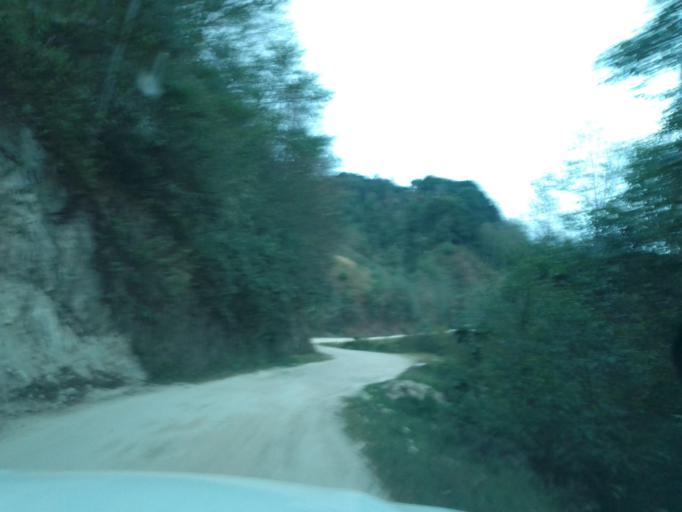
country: MX
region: Chiapas
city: Motozintla de Mendoza
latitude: 15.2280
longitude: -92.2382
